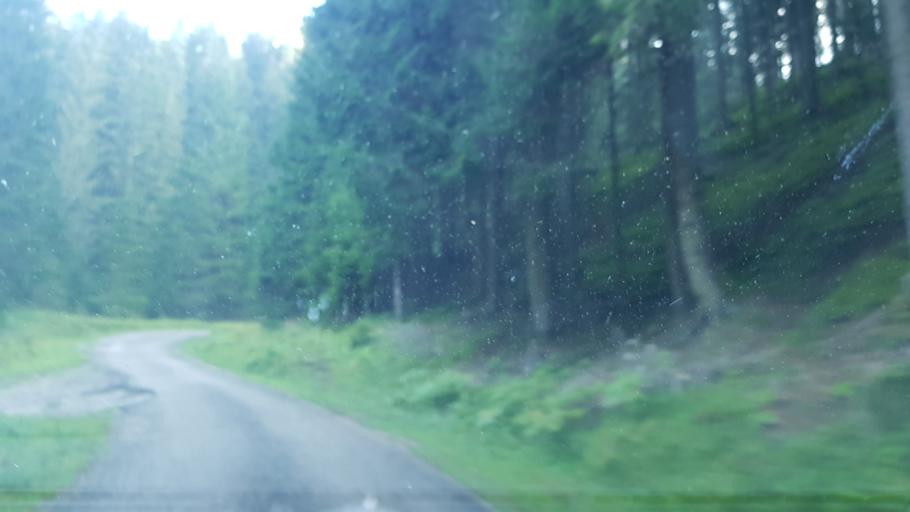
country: IT
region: Veneto
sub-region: Provincia di Belluno
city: San Pietro di Cadore
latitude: 46.5972
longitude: 12.5804
